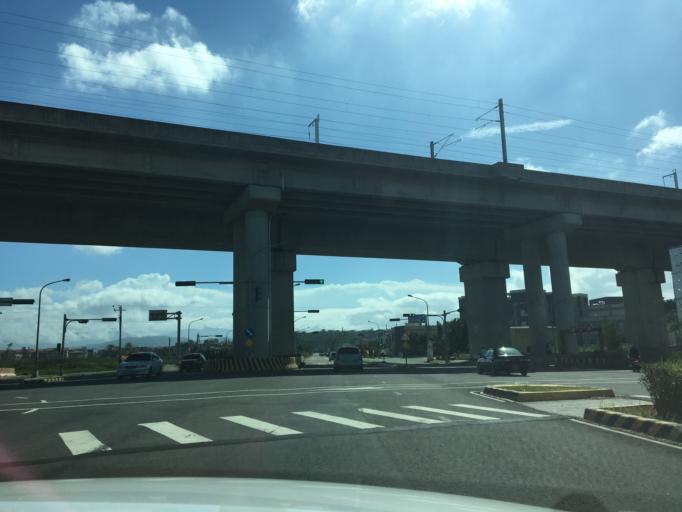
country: TW
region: Taiwan
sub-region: Hsinchu
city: Zhubei
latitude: 24.7857
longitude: 121.0342
